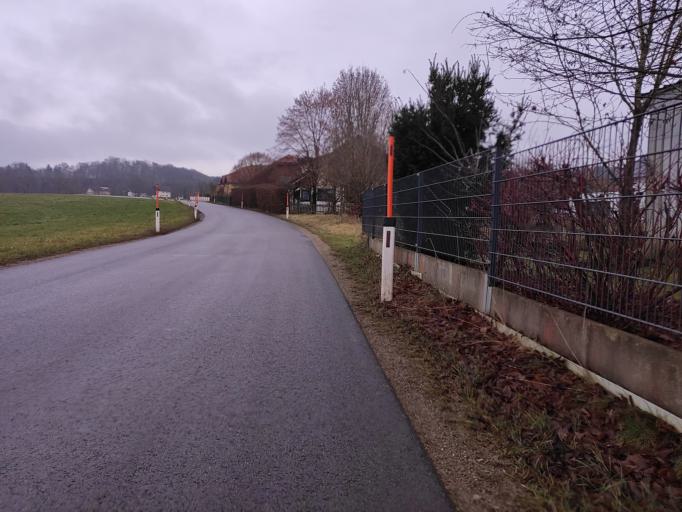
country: AT
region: Salzburg
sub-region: Politischer Bezirk Salzburg-Umgebung
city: Henndorf am Wallersee
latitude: 47.8958
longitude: 13.1594
